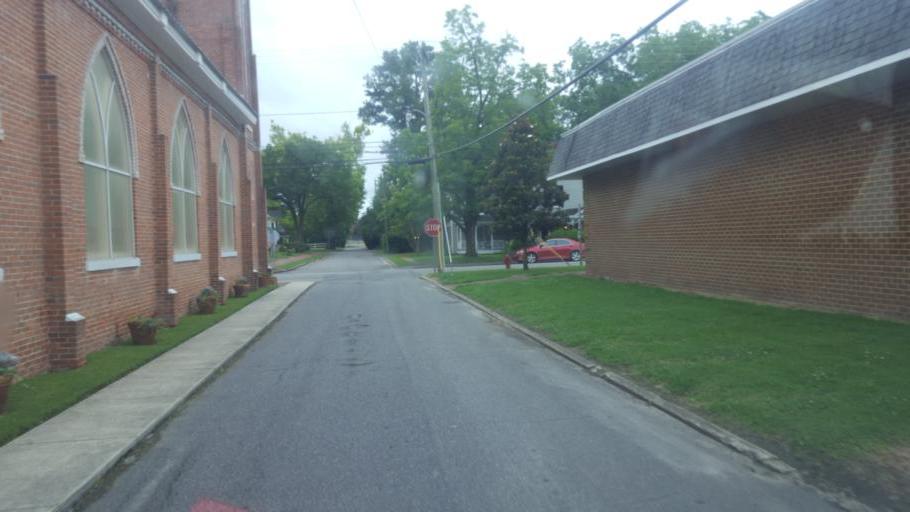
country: US
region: North Carolina
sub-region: Tyrrell County
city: Columbia
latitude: 35.9184
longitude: -76.2509
